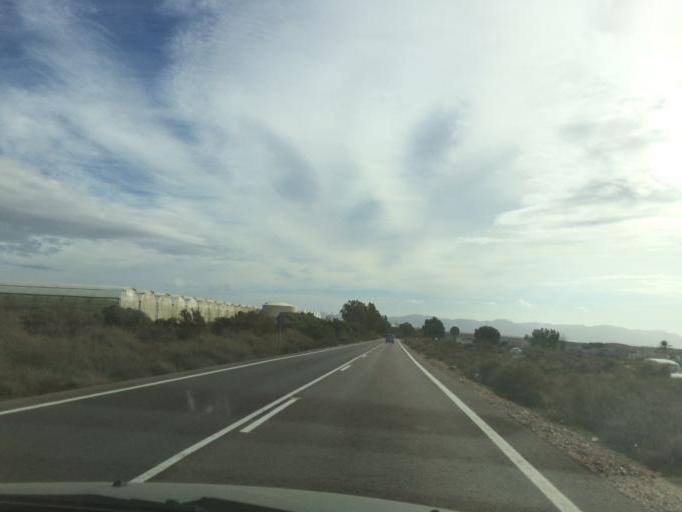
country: ES
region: Andalusia
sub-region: Provincia de Almeria
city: Retamar
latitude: 36.8380
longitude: -2.2918
